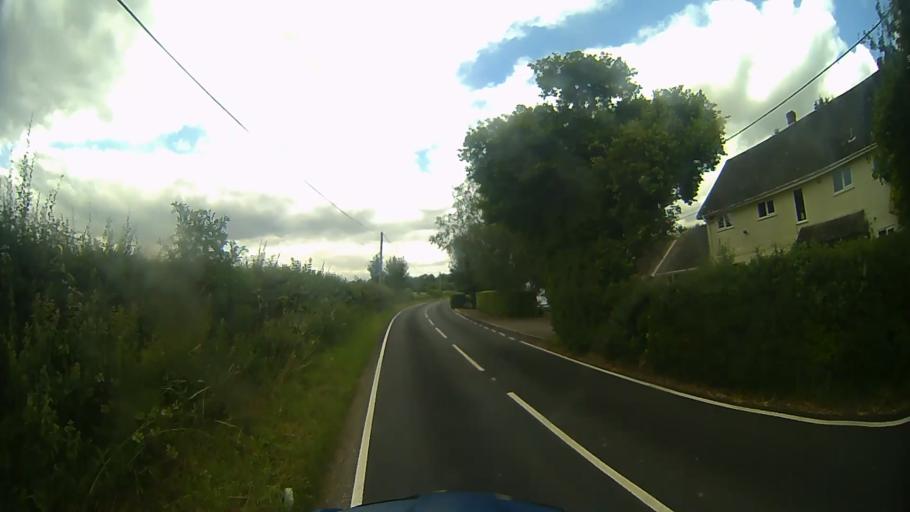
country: GB
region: England
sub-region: Hampshire
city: Four Marks
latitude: 51.1082
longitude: -1.1604
